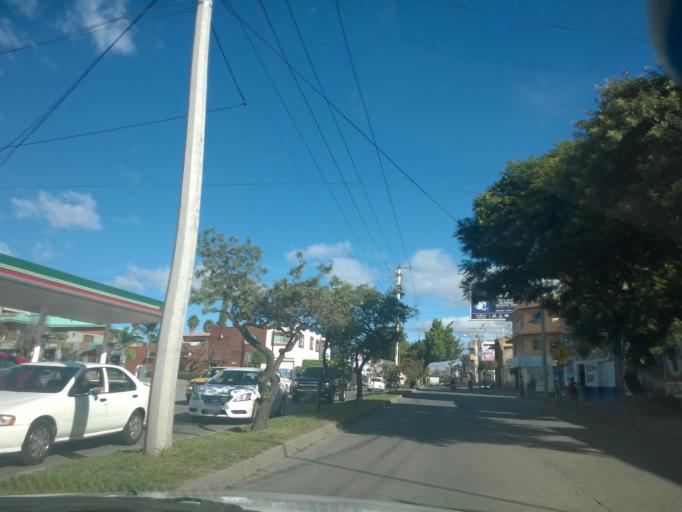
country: MX
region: Guanajuato
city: Leon
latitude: 21.1168
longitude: -101.7009
